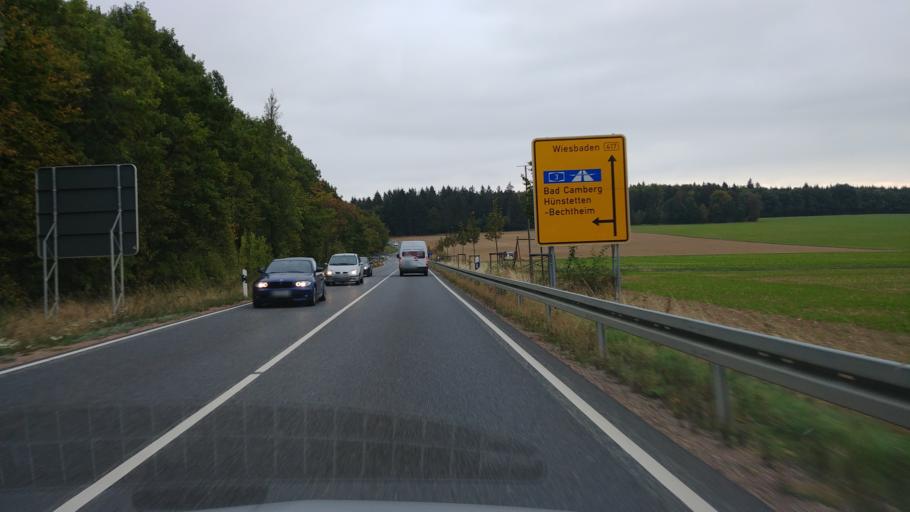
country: DE
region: Rheinland-Pfalz
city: Kaltenholzhausen
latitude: 50.2682
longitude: 8.1714
